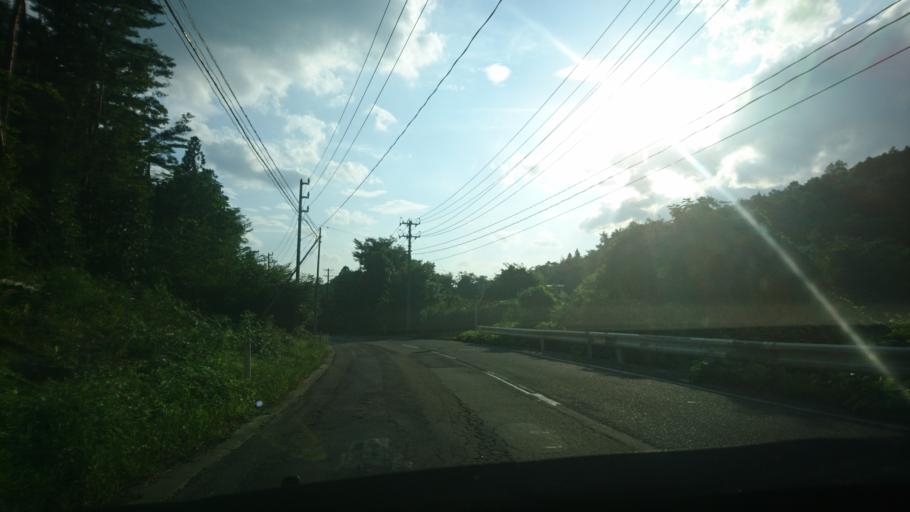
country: JP
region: Iwate
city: Ichinoseki
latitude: 38.9973
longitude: 141.2778
